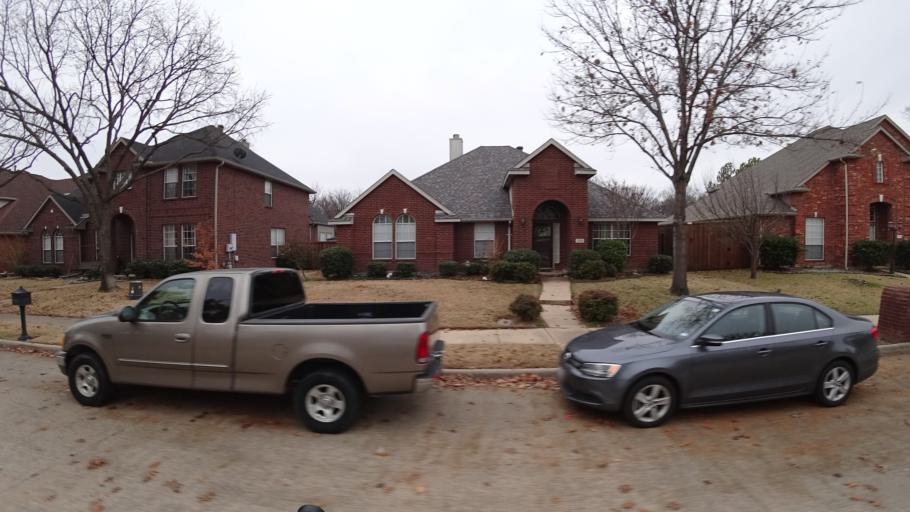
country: US
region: Texas
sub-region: Denton County
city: Lewisville
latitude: 33.0554
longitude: -97.0252
